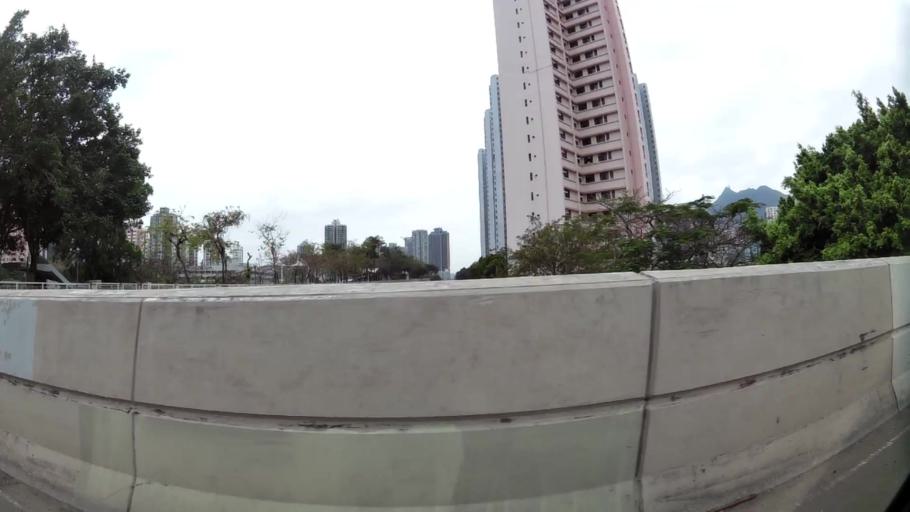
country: HK
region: Tuen Mun
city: Tuen Mun
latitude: 22.4057
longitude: 113.9764
